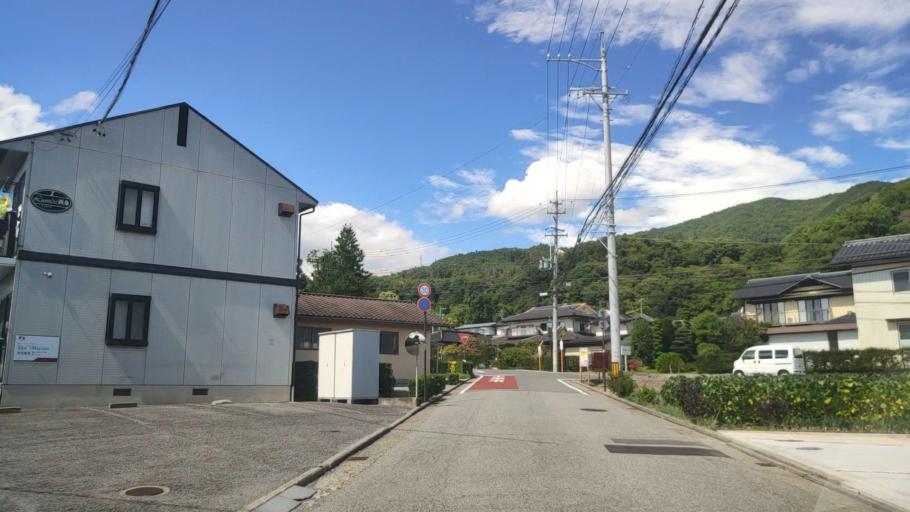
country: JP
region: Nagano
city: Nagano-shi
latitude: 36.6879
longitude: 138.2174
